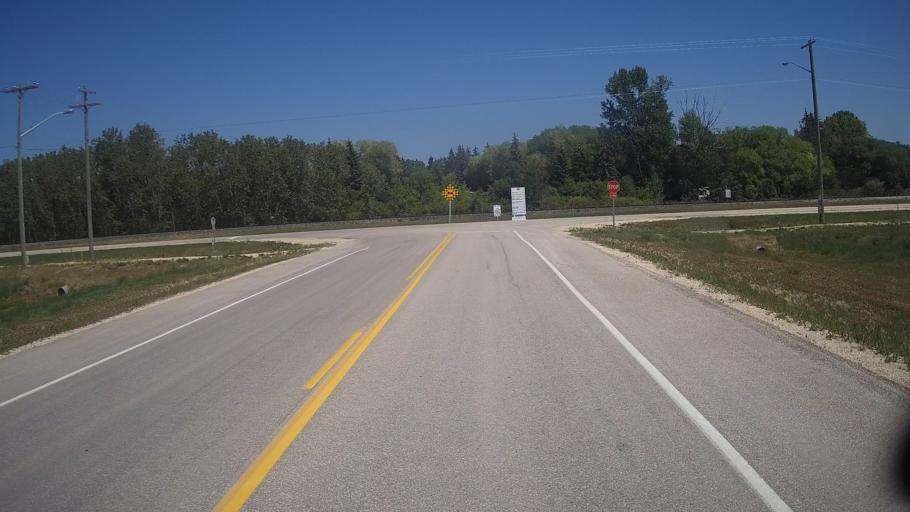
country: CA
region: Manitoba
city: Stonewall
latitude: 50.1286
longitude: -97.5423
